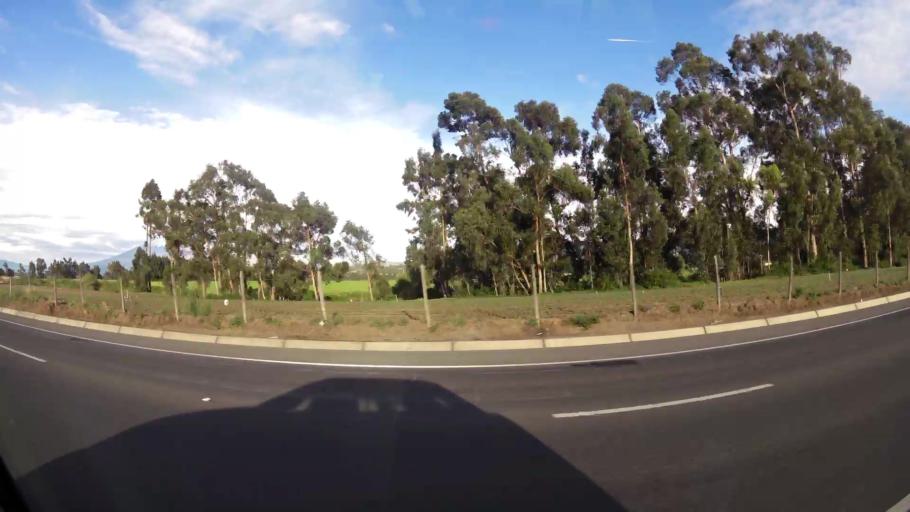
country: EC
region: Cotopaxi
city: Saquisili
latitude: -0.8359
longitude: -78.6191
